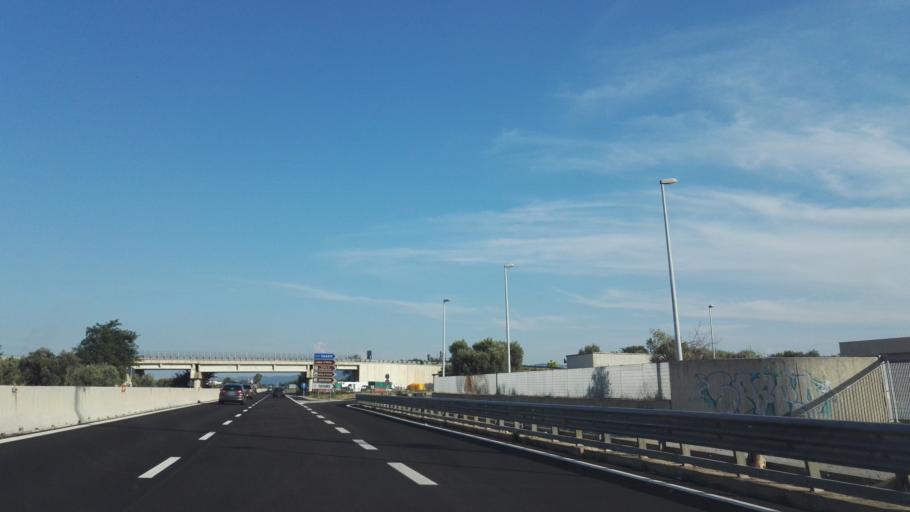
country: IT
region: Apulia
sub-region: Provincia di Brindisi
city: Fasano
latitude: 40.8523
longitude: 17.3561
